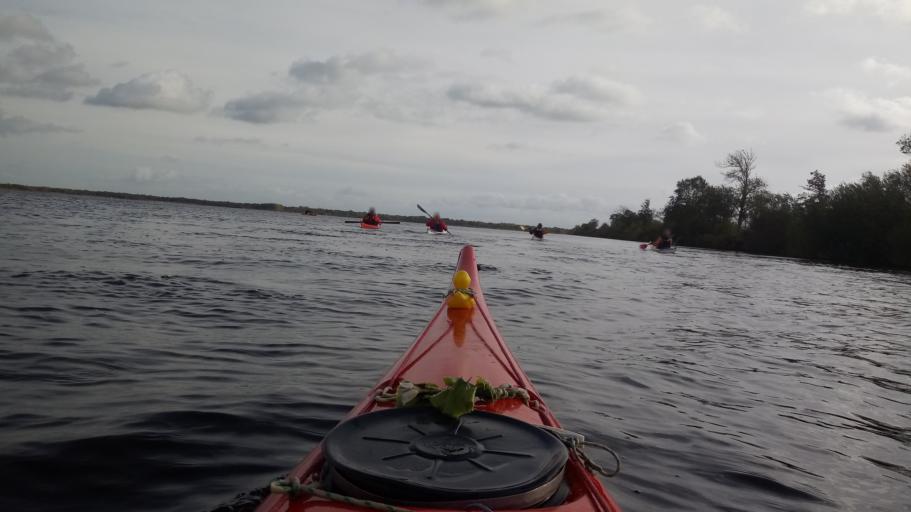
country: NL
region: Overijssel
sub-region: Gemeente Steenwijkerland
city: Wanneperveen
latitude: 52.6903
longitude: 6.0763
